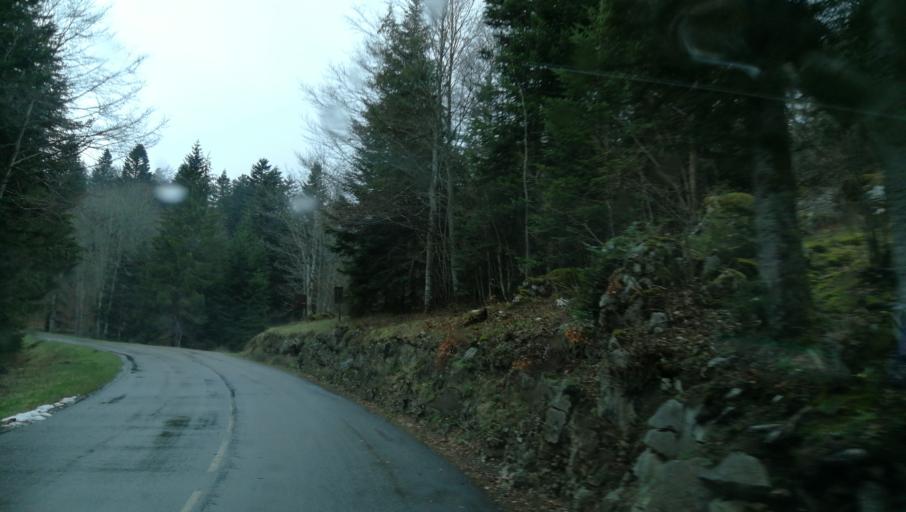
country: FR
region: Rhone-Alpes
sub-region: Departement de la Drome
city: Saint-Jean-en-Royans
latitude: 44.9608
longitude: 5.3297
